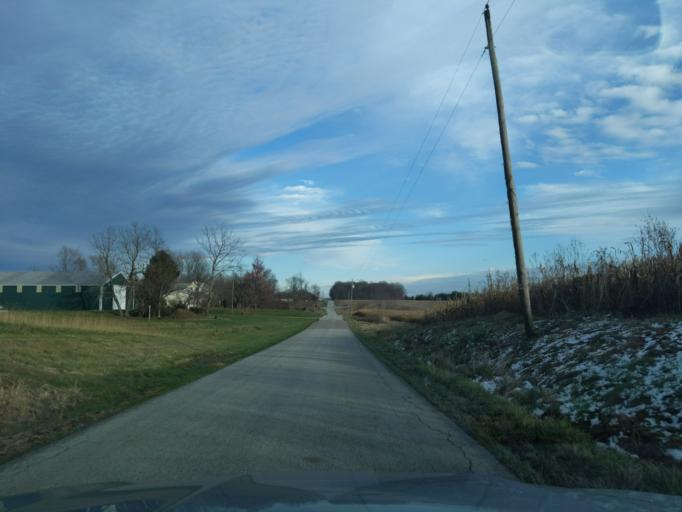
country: US
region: Indiana
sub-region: Decatur County
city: Westport
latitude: 39.2192
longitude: -85.4831
